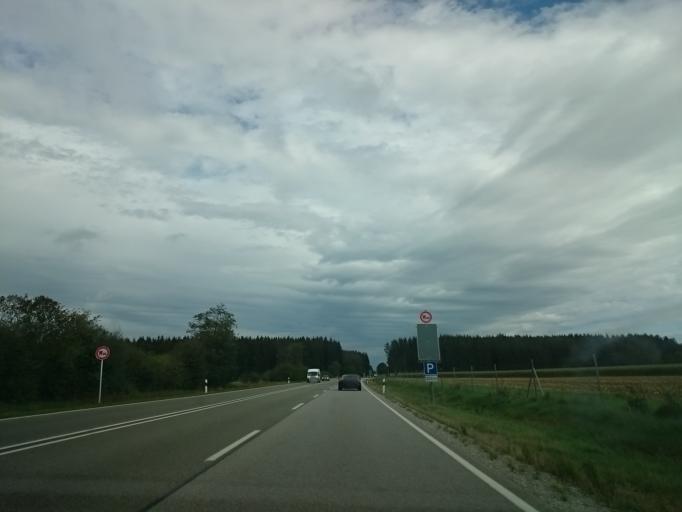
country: DE
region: Bavaria
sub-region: Swabia
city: Jengen
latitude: 47.9780
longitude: 10.6915
